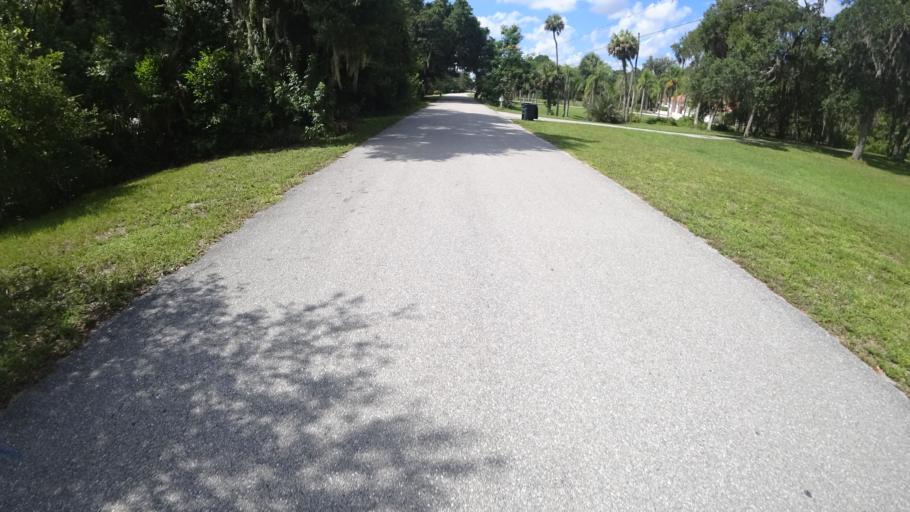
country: US
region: Florida
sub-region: Manatee County
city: Samoset
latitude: 27.4676
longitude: -82.4829
